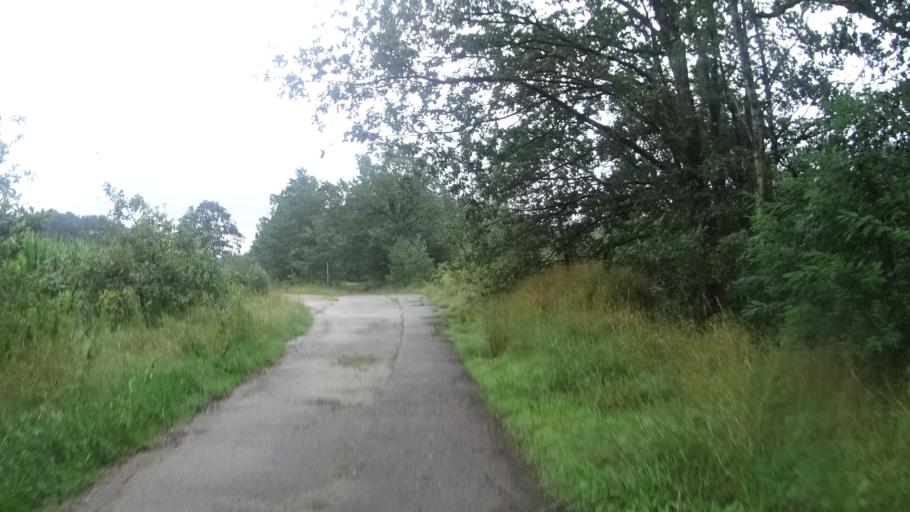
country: DE
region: Schleswig-Holstein
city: Siebeneichen
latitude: 53.5001
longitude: 10.6157
